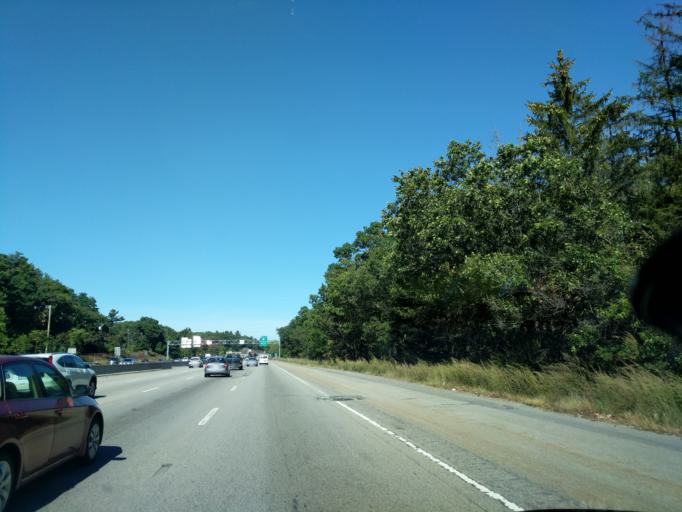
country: US
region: Massachusetts
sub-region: Middlesex County
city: Waltham
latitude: 42.3523
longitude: -71.2649
